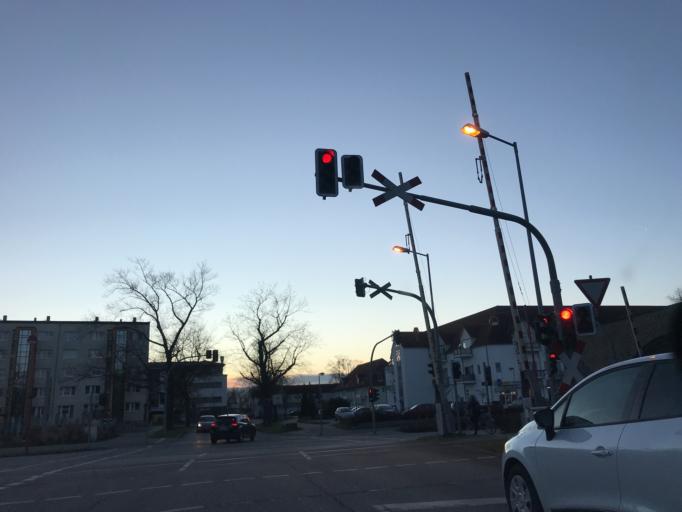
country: DE
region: Brandenburg
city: Premnitz
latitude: 52.5299
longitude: 12.3423
